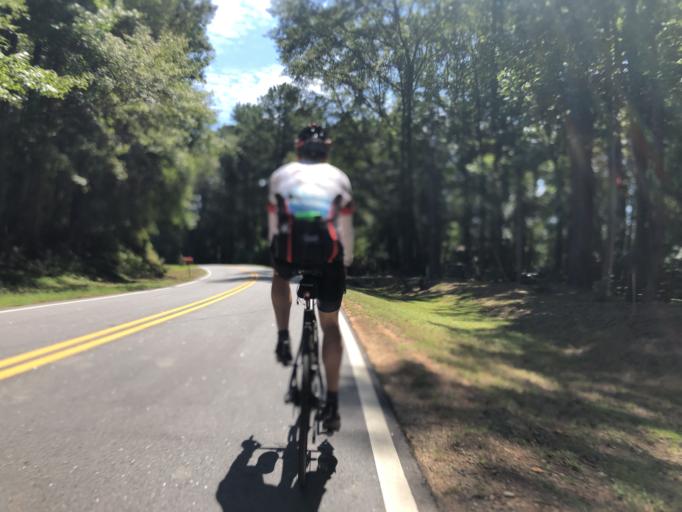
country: US
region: Georgia
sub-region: Fulton County
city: Chattahoochee Hills
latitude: 33.4809
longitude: -84.8103
